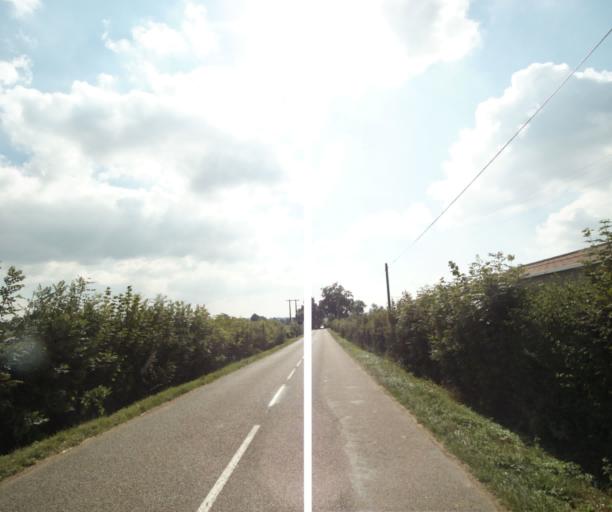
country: FR
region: Bourgogne
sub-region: Departement de Saone-et-Loire
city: Charolles
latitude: 46.3782
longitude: 4.2495
